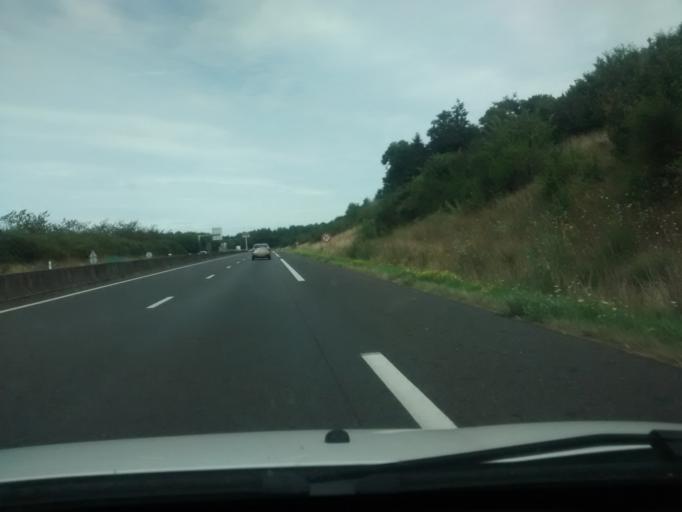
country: FR
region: Brittany
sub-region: Departement d'Ille-et-Vilaine
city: Saint-Etienne-en-Cogles
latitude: 48.3985
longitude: -1.3092
